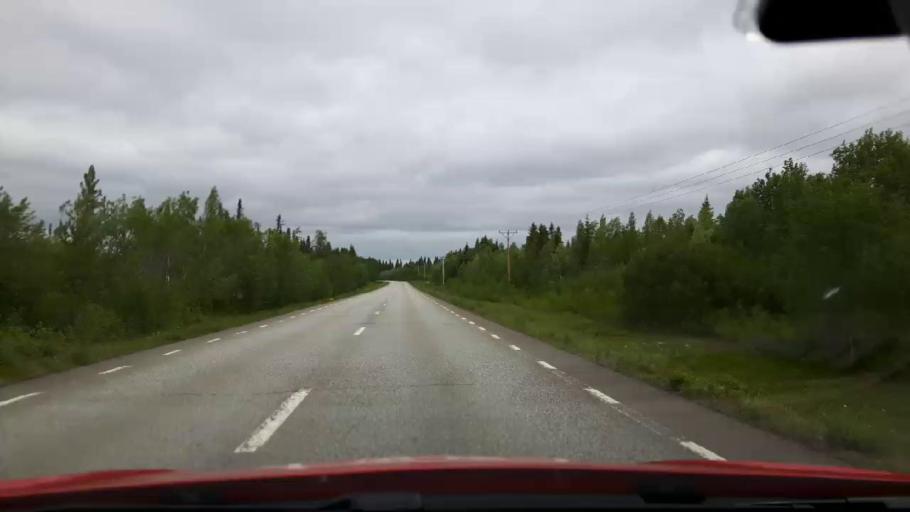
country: SE
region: Jaemtland
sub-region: Krokoms Kommun
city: Krokom
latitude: 63.5681
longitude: 14.6198
